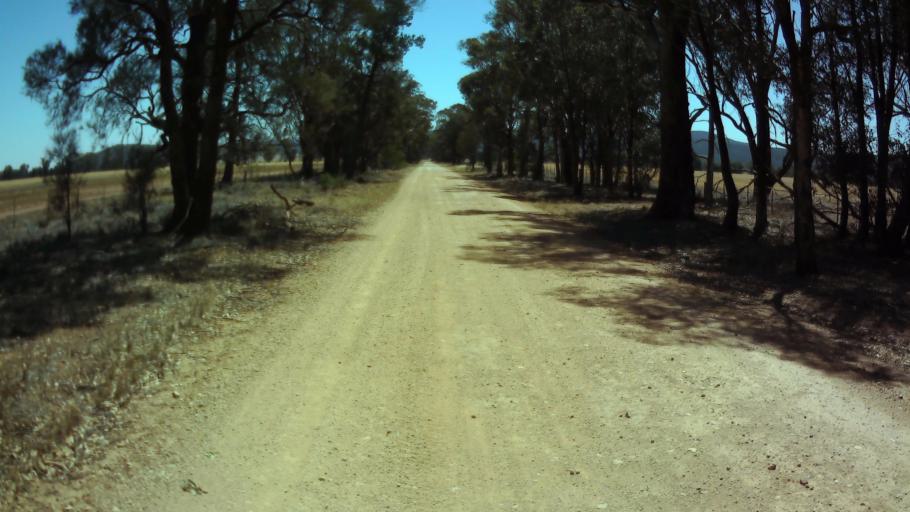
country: AU
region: New South Wales
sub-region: Weddin
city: Grenfell
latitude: -34.0152
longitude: 147.9629
